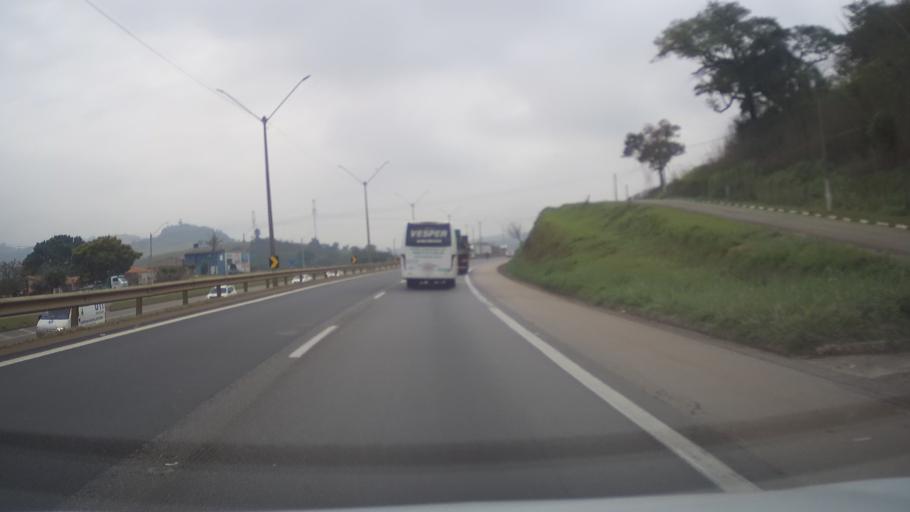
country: BR
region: Sao Paulo
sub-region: Atibaia
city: Atibaia
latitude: -23.0374
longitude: -46.5544
